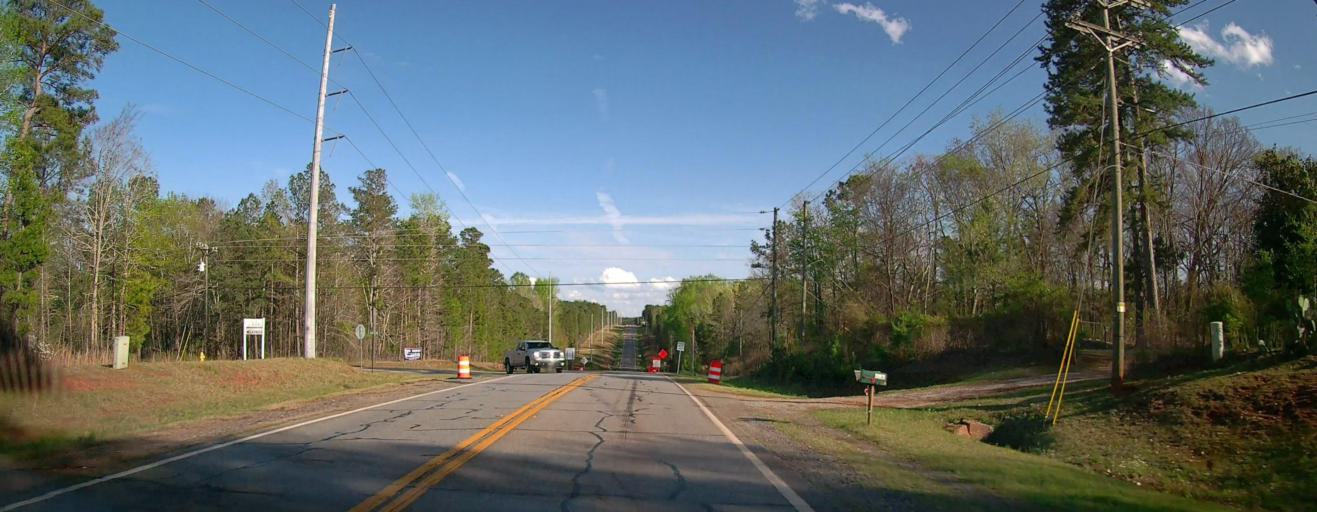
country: US
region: Georgia
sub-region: Baldwin County
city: Milledgeville
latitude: 33.1368
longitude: -83.3269
